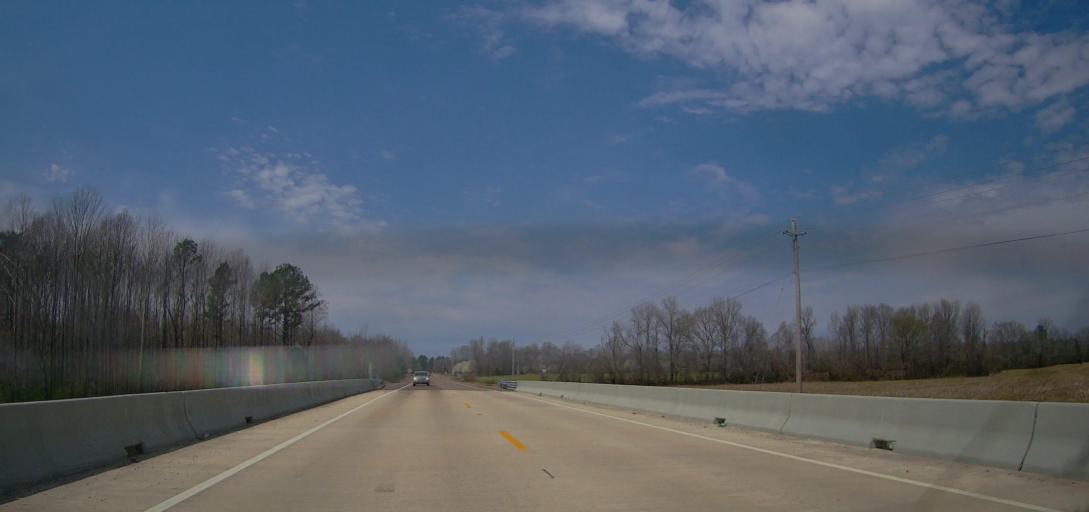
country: US
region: Mississippi
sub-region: Union County
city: New Albany
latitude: 34.6157
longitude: -89.1648
